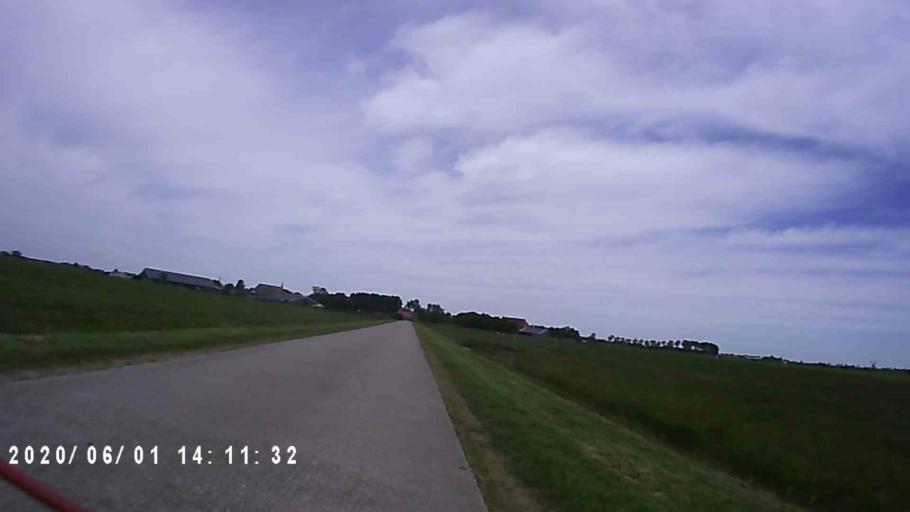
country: NL
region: Friesland
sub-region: Gemeente Littenseradiel
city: Winsum
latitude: 53.1273
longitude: 5.6495
